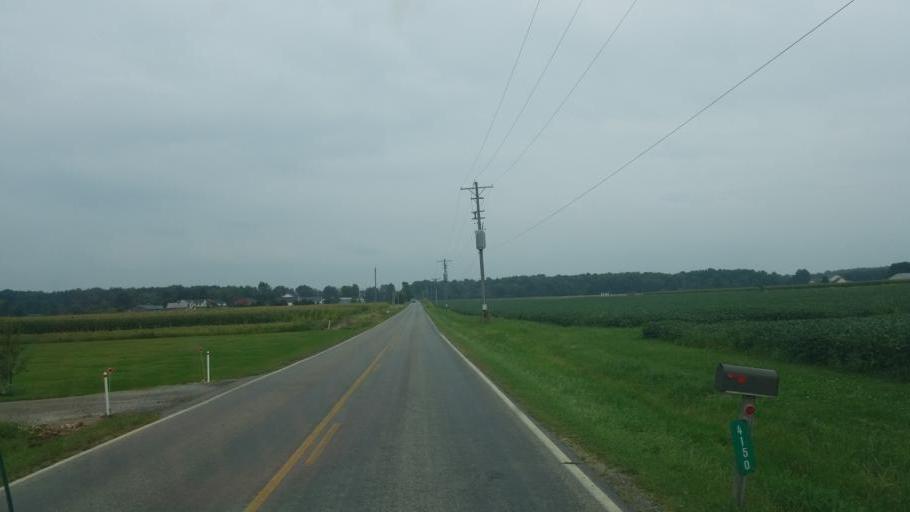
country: US
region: Ohio
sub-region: Wayne County
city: Creston
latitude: 40.9602
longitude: -81.8905
